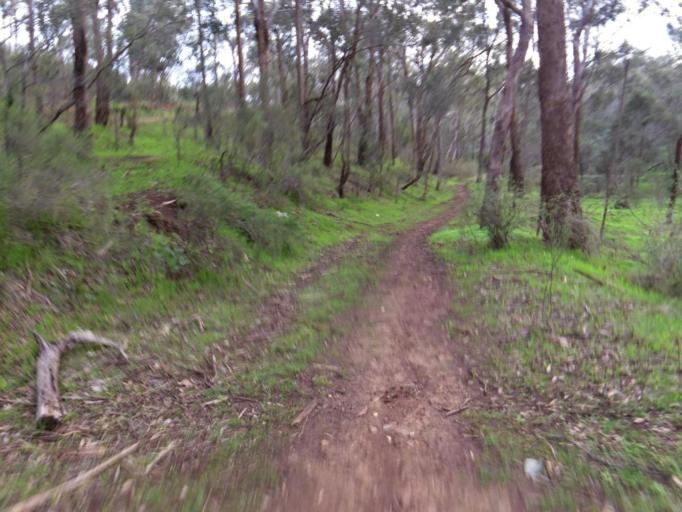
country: AU
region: Victoria
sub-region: Whittlesea
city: Mill Park
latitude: -37.6718
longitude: 145.0906
